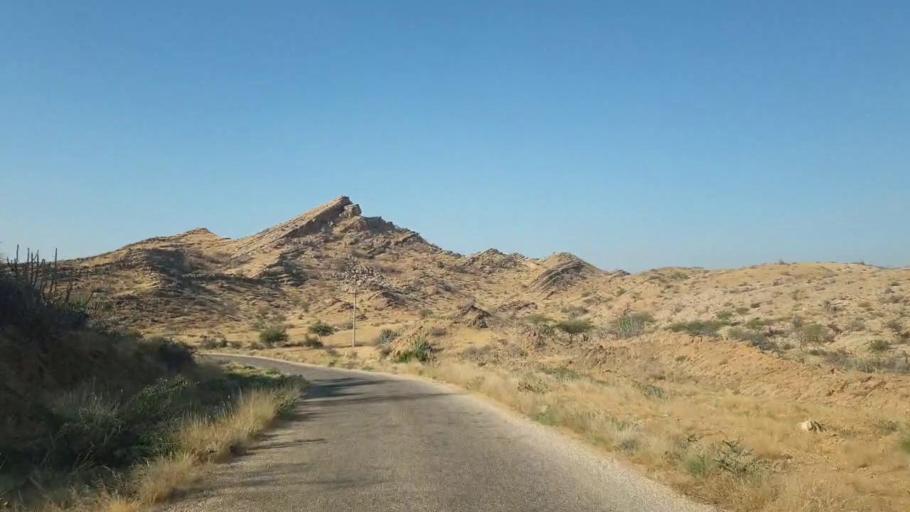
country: PK
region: Sindh
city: Malir Cantonment
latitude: 25.4042
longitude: 67.4848
